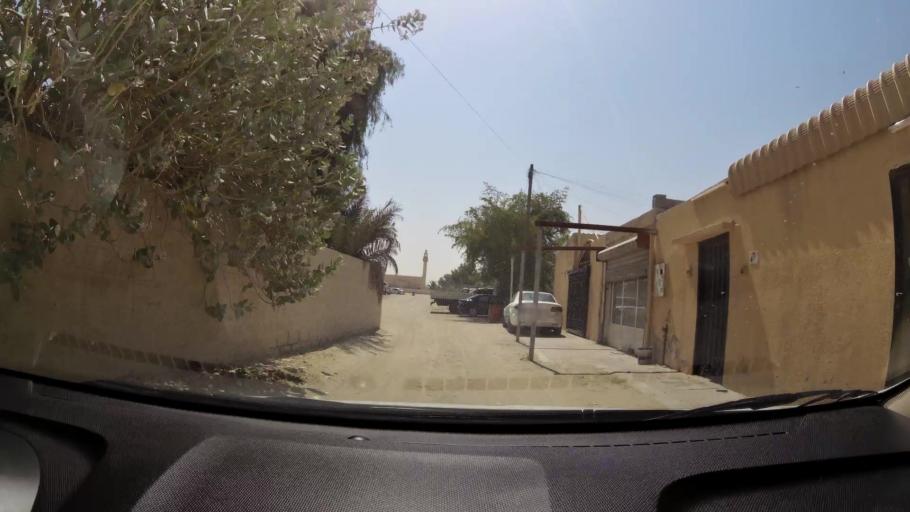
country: AE
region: Ajman
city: Ajman
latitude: 25.3962
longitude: 55.5270
